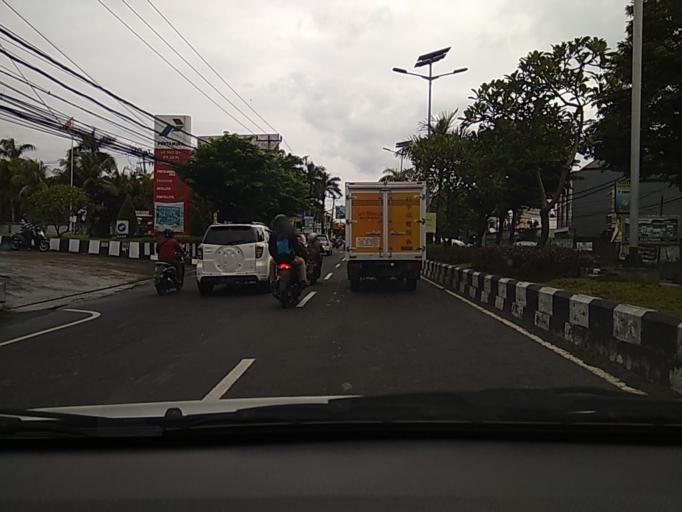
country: ID
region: Bali
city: Jimbaran
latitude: -8.7840
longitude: 115.1884
